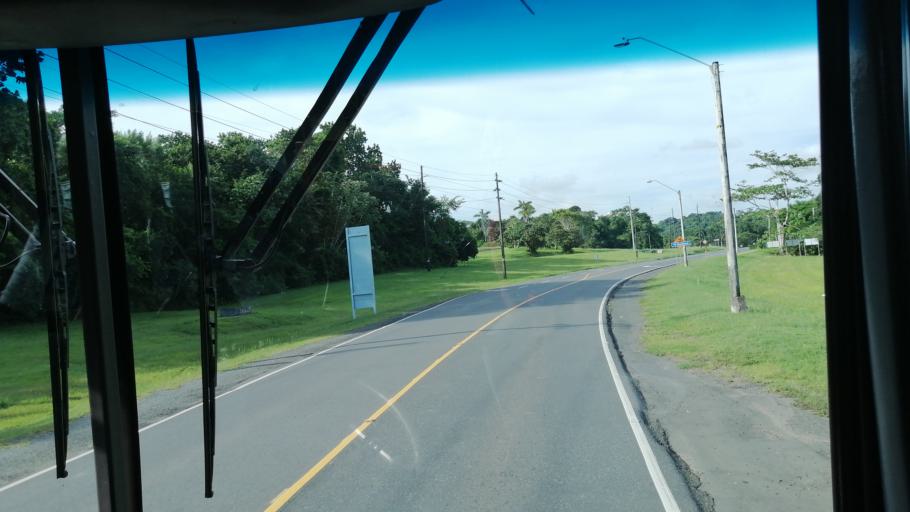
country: PA
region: Panama
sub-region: Distrito de Panama
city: Ancon
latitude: 8.9293
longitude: -79.5923
